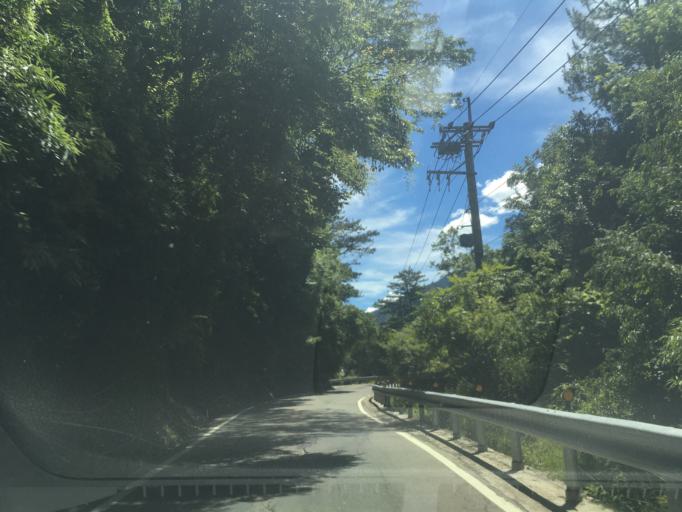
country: TW
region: Taiwan
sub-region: Nantou
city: Puli
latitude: 24.2439
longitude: 121.2547
